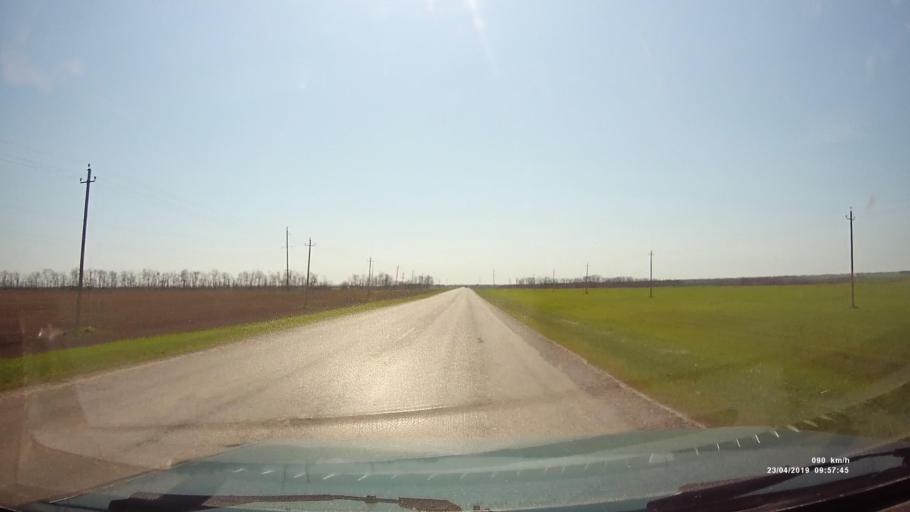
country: RU
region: Rostov
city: Sovetskoye
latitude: 46.7859
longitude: 42.0900
